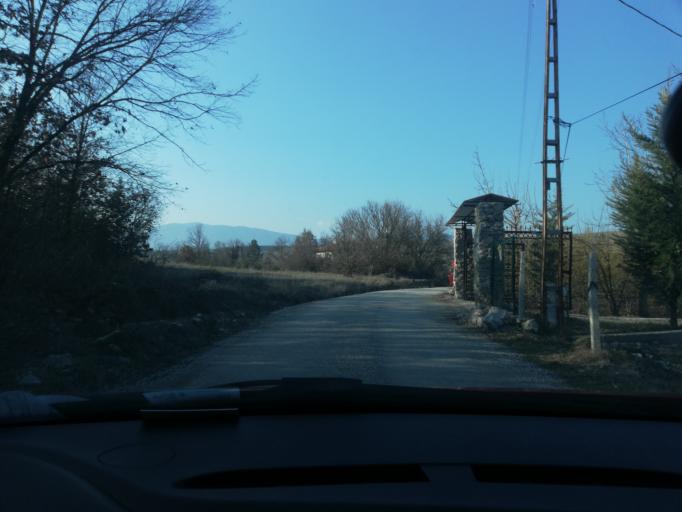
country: TR
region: Karabuk
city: Safranbolu
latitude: 41.2148
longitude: 32.7458
